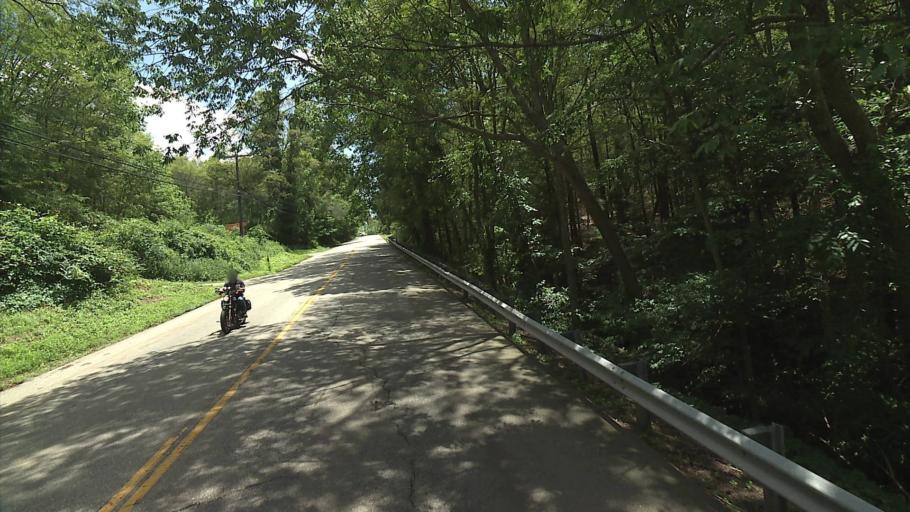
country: US
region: Connecticut
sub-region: Middlesex County
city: Moodus
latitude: 41.5100
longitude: -72.4800
